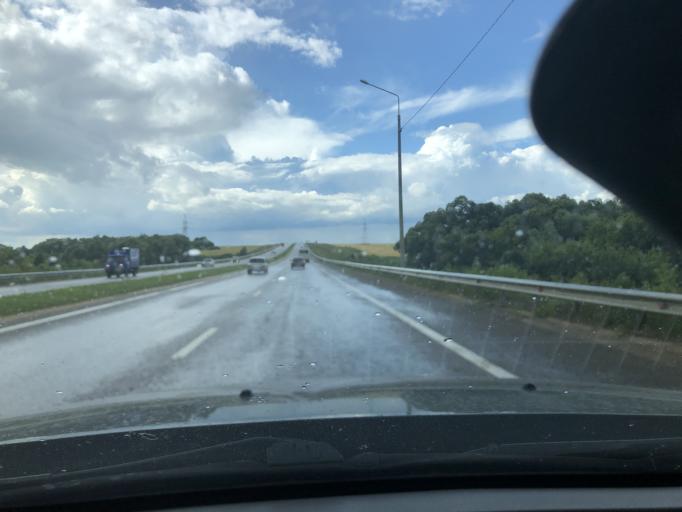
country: RU
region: Tula
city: Kamenetskiy
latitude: 54.0405
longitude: 38.2048
